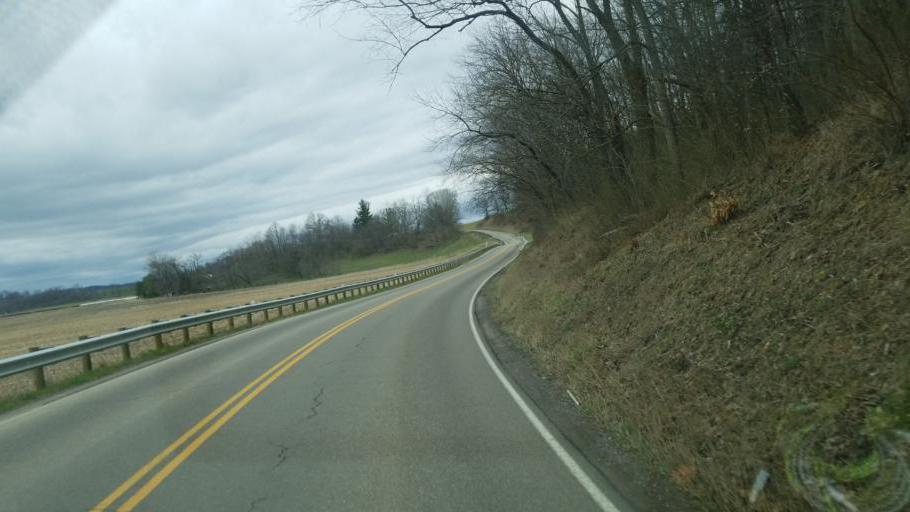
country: US
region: Ohio
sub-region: Holmes County
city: Millersburg
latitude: 40.6222
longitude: -81.8841
